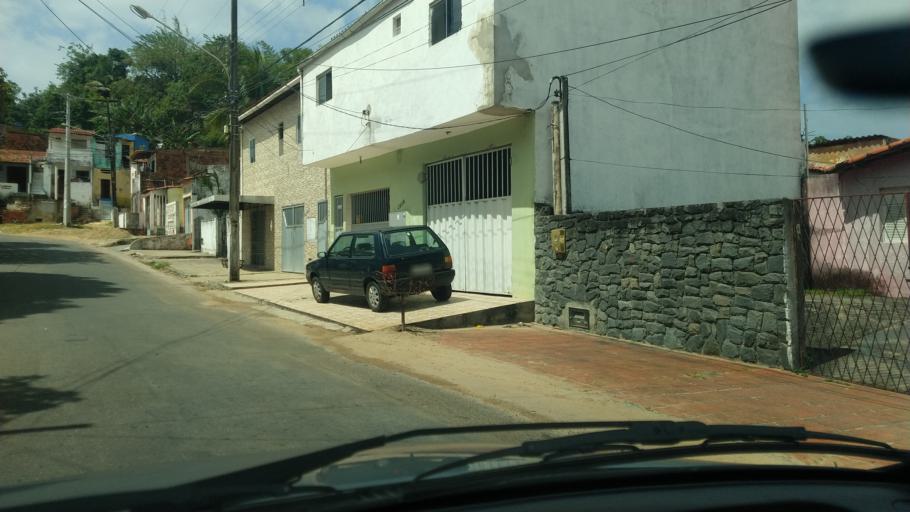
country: BR
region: Rio Grande do Norte
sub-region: Parnamirim
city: Parnamirim
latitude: -5.8727
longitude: -35.2122
